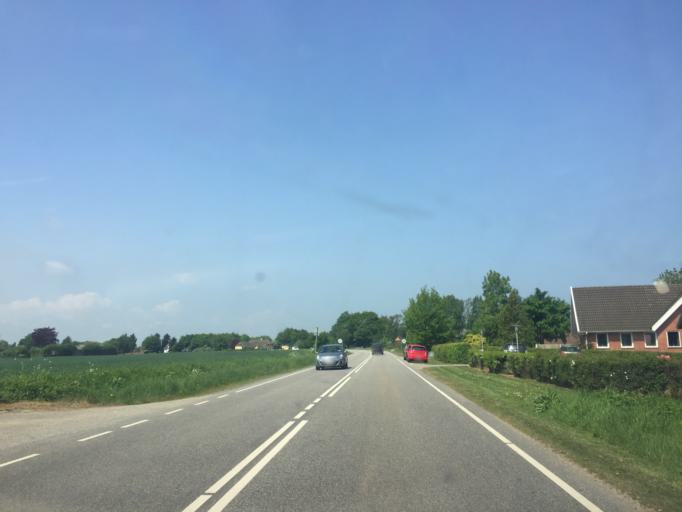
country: DK
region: South Denmark
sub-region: Kolding Kommune
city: Sonder Bjert
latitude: 55.3692
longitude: 9.6009
